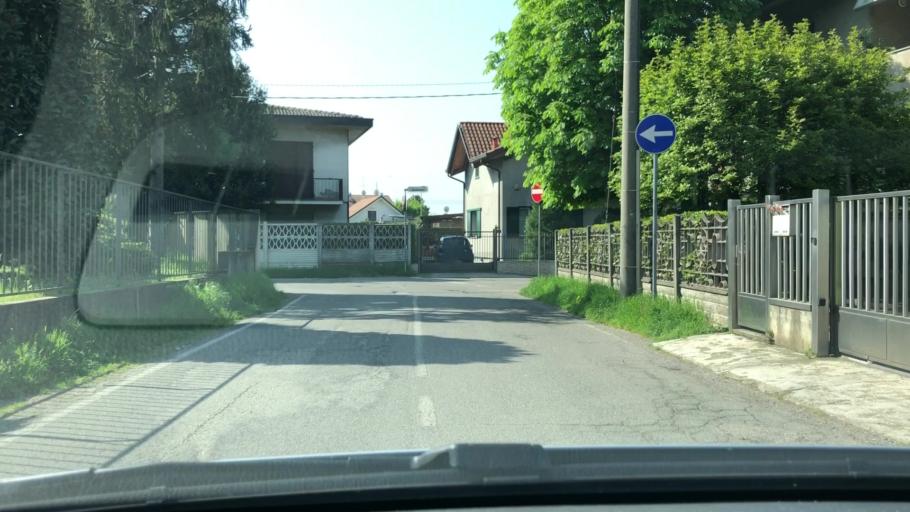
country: IT
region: Lombardy
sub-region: Provincia di Monza e Brianza
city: Barlassina
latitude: 45.6444
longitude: 9.1270
